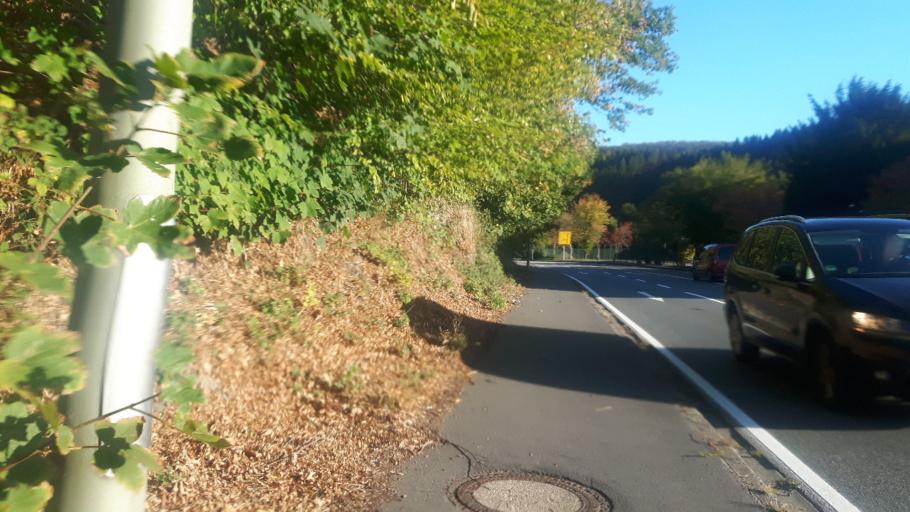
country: DE
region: Rheinland-Pfalz
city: Kirchen
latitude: 50.8181
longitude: 7.8920
